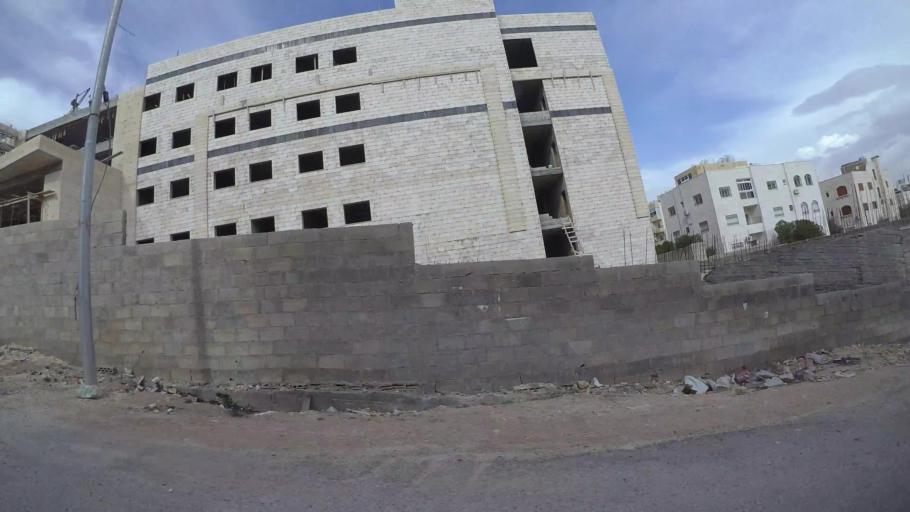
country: JO
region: Amman
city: Amman
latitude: 32.0130
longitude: 35.9389
